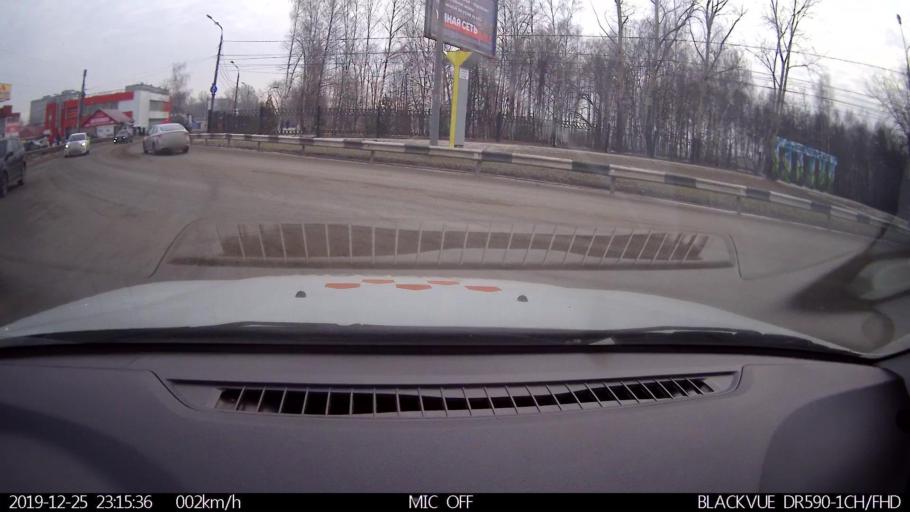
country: RU
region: Nizjnij Novgorod
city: Gorbatovka
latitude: 56.3592
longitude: 43.8260
